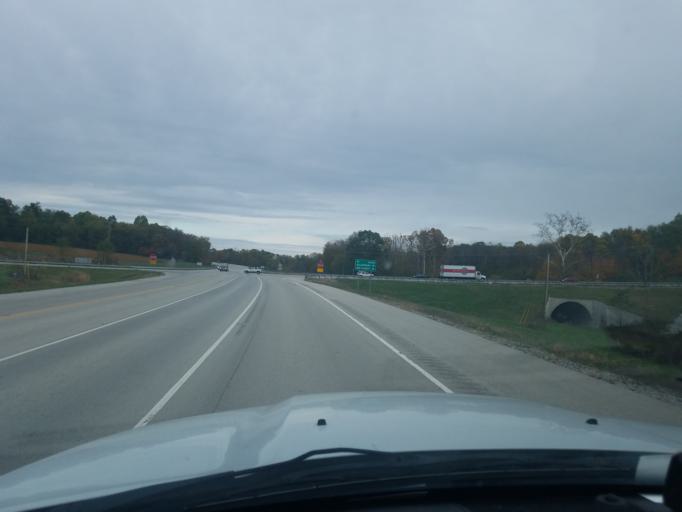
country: US
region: Indiana
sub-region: Washington County
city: Salem
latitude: 38.5876
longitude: -86.0698
